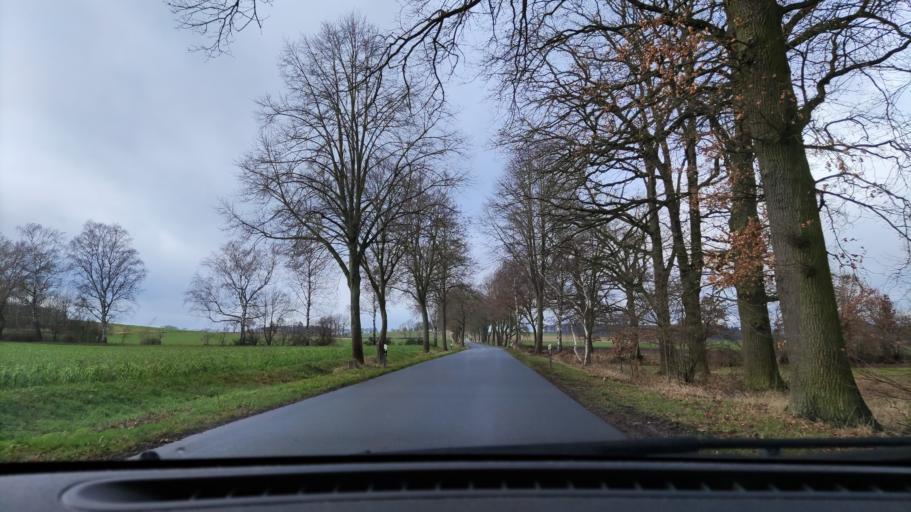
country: DE
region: Lower Saxony
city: Jelmstorf
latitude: 53.0800
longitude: 10.5085
